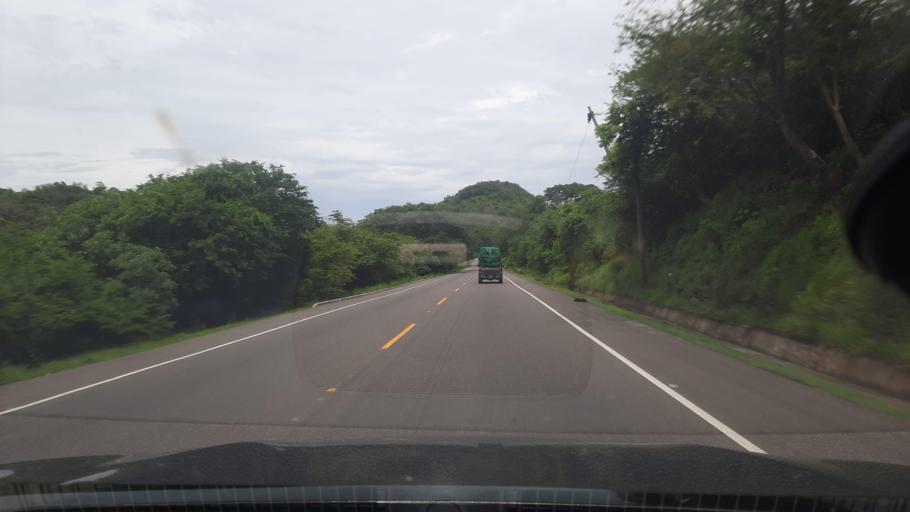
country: HN
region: Valle
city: Langue
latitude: 13.5736
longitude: -87.6750
